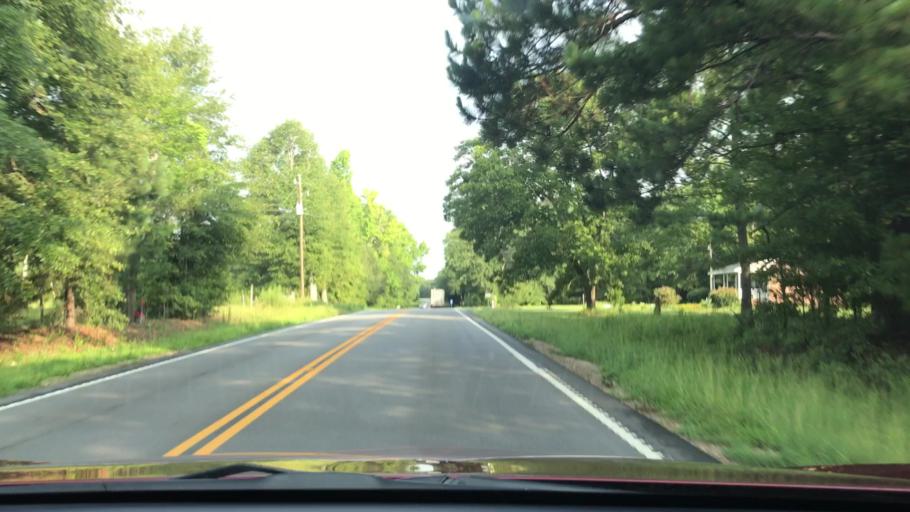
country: US
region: South Carolina
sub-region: Bamberg County
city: Denmark
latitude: 33.5403
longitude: -81.1388
